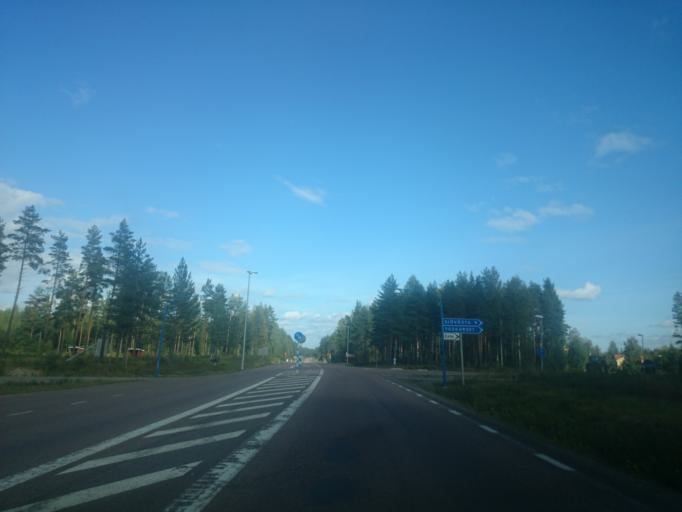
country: SE
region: Gaevleborg
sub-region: Ljusdals Kommun
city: Farila
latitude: 61.8008
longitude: 15.8935
